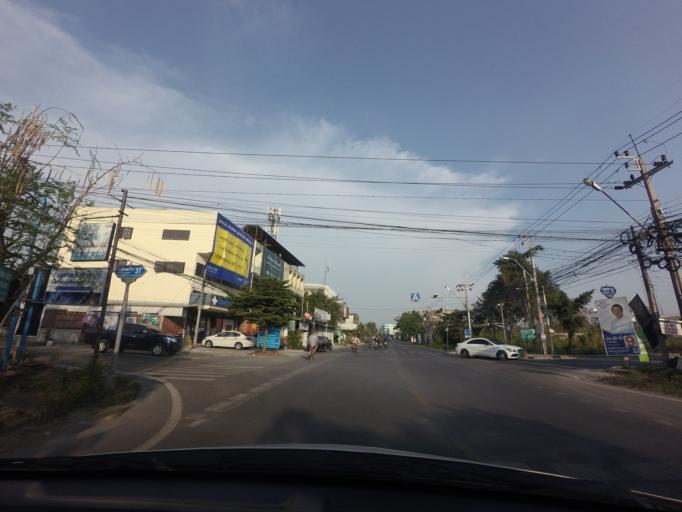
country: TH
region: Bangkok
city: Saphan Sung
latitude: 13.7415
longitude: 100.6825
